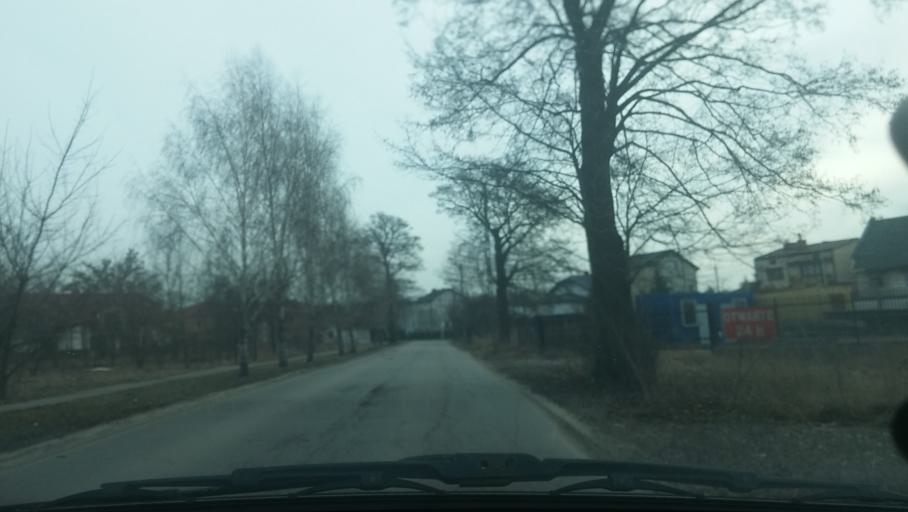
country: PL
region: Masovian Voivodeship
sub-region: Powiat wolominski
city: Zabki
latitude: 52.3046
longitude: 21.0999
